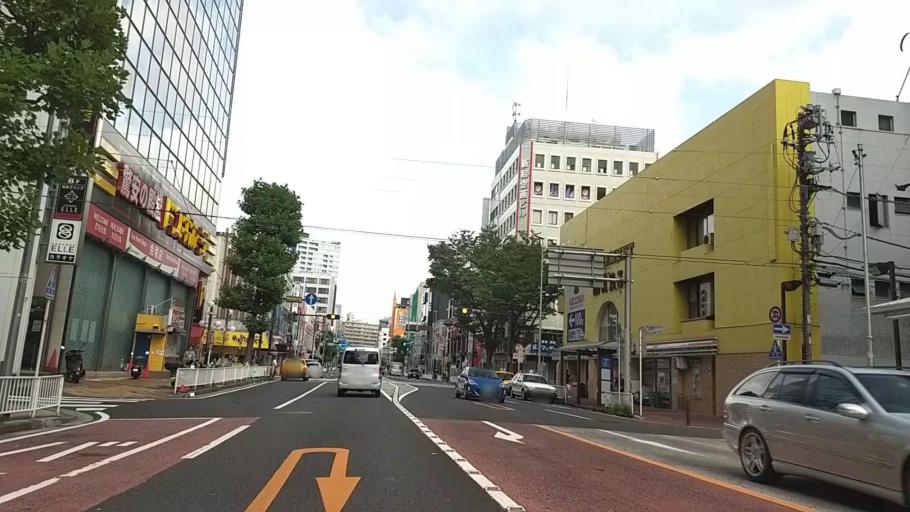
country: JP
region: Kanagawa
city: Yokohama
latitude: 35.4425
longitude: 139.6312
